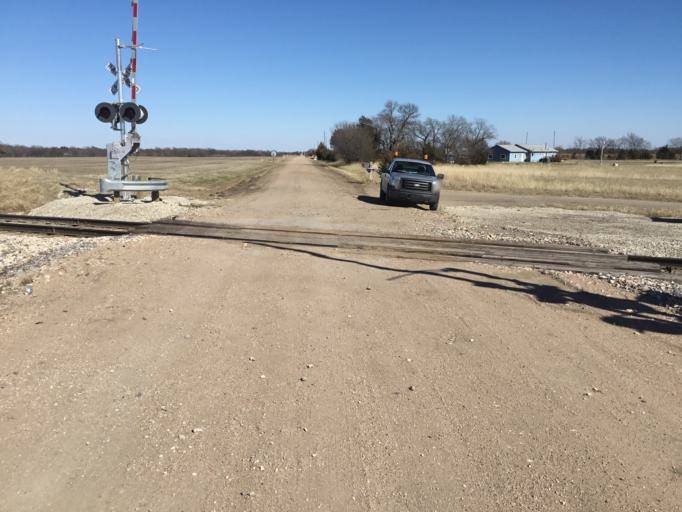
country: US
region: Kansas
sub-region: Sedgwick County
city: Kechi
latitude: 37.8982
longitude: -97.2007
